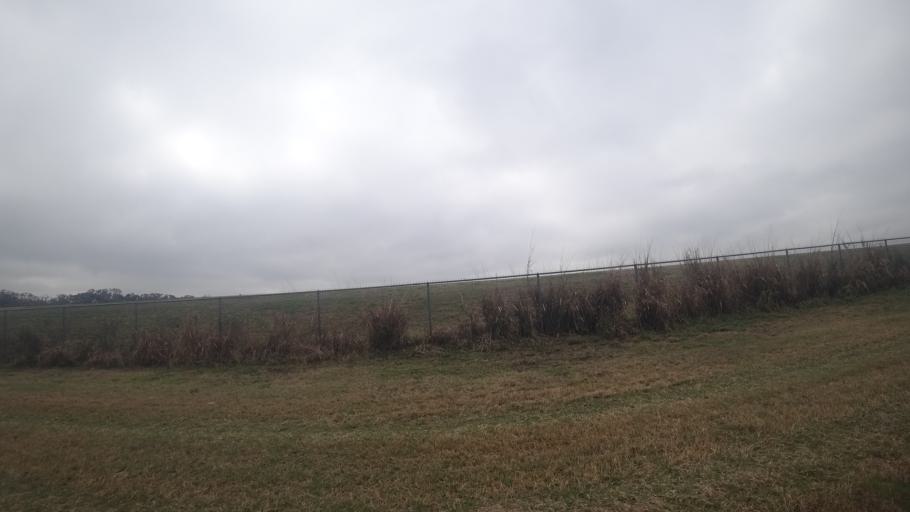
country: US
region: Florida
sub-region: Manatee County
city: Ellenton
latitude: 27.5894
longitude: -82.4815
